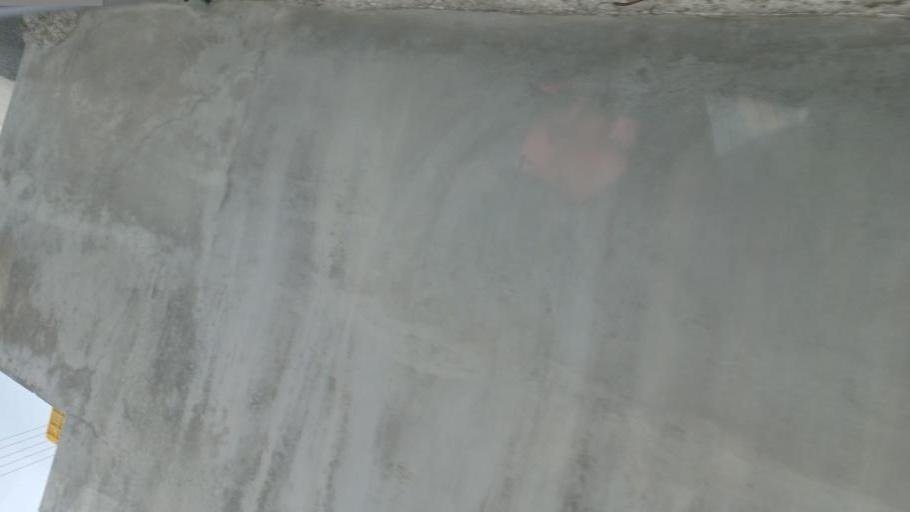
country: CY
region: Pafos
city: Mesogi
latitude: 34.8574
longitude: 32.5154
